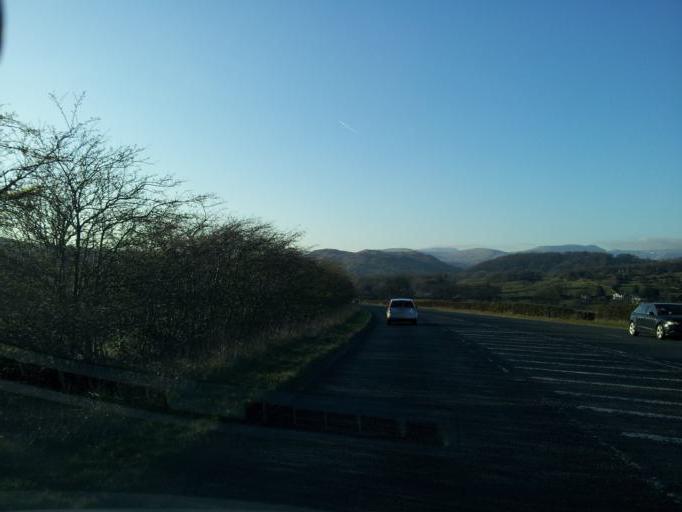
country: GB
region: England
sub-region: Cumbria
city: Kendal
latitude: 54.3586
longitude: -2.7872
